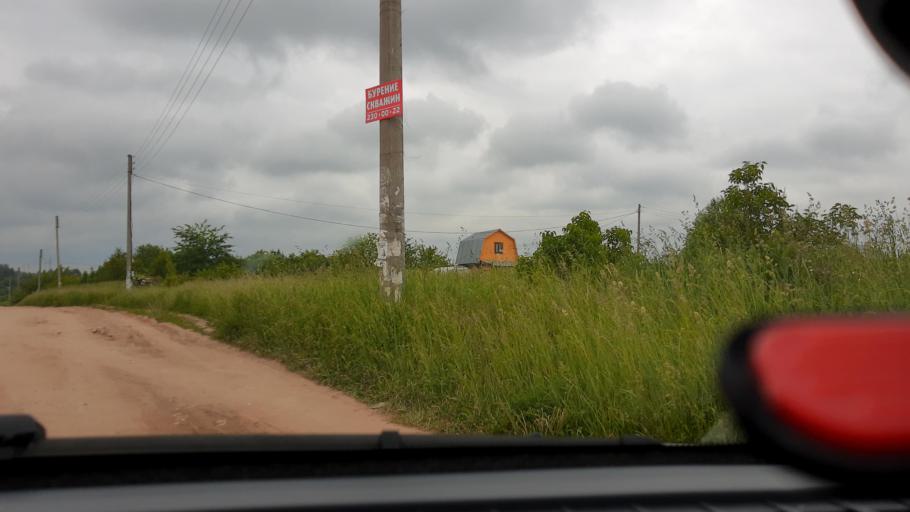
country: RU
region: Nizjnij Novgorod
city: Burevestnik
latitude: 56.1028
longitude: 43.9377
